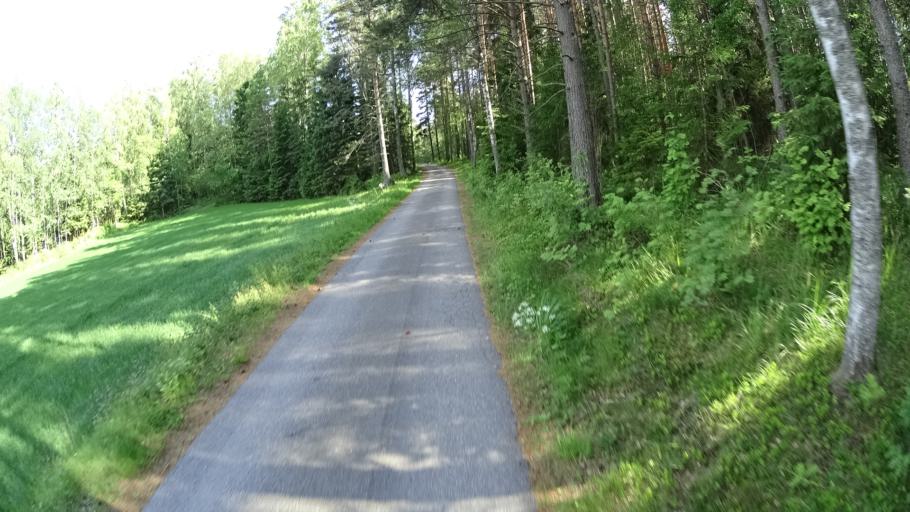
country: FI
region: Uusimaa
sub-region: Helsinki
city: Vantaa
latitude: 60.2358
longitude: 25.1827
